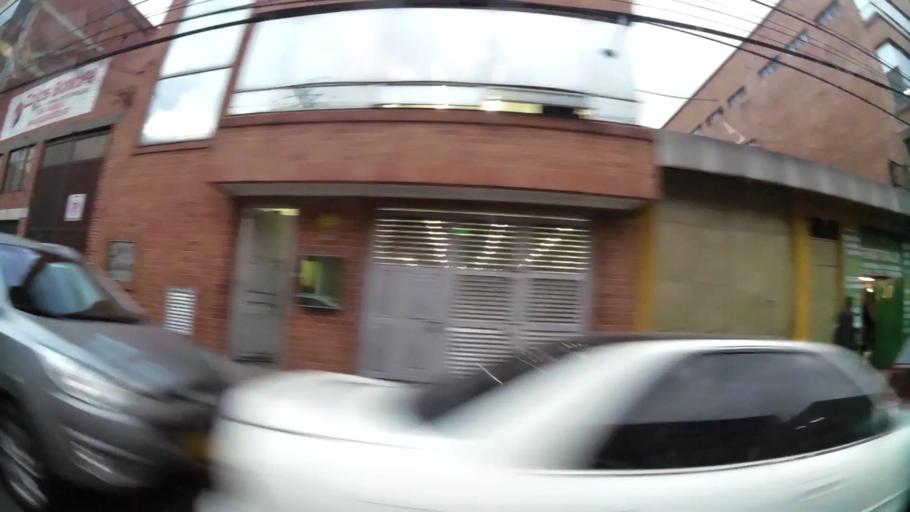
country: CO
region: Bogota D.C.
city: Bogota
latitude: 4.6095
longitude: -74.0920
